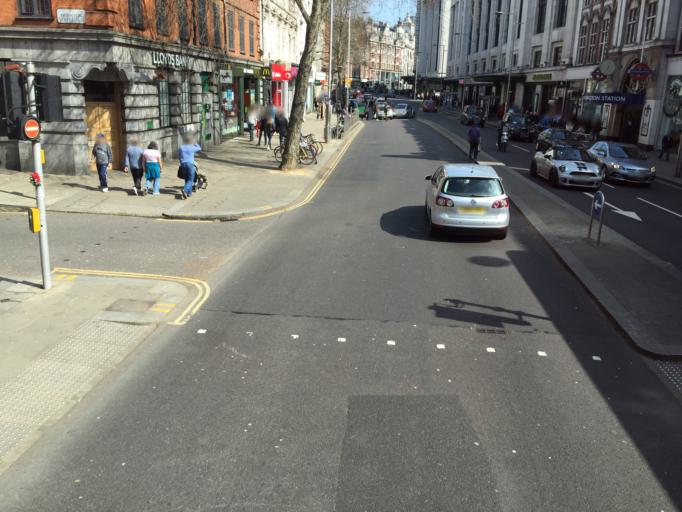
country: GB
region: England
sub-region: Greater London
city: Kensington
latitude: 51.5010
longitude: -0.1934
